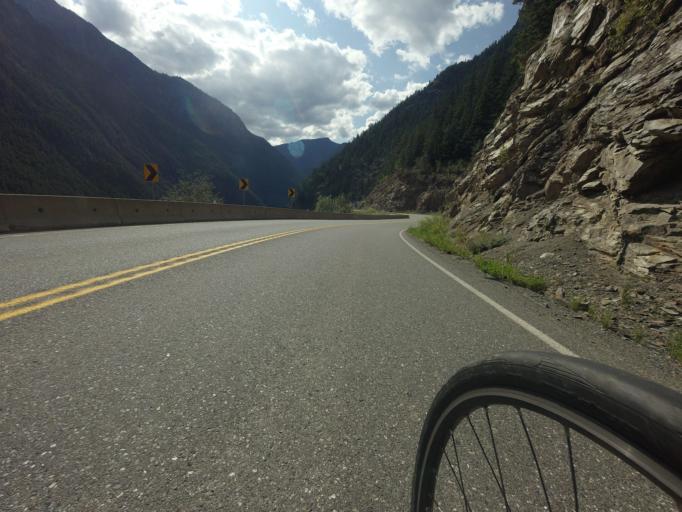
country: CA
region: British Columbia
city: Lillooet
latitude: 50.6420
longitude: -122.0278
